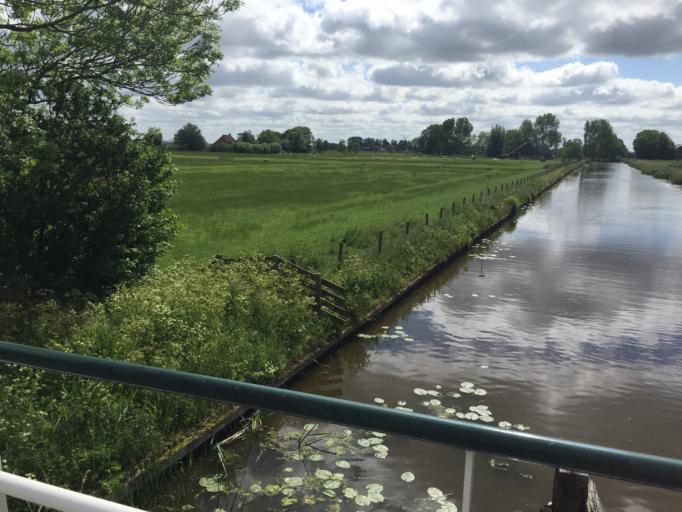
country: NL
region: Friesland
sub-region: Gemeente Ferwerderadiel
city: Burdaard
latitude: 53.2790
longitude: 5.8364
